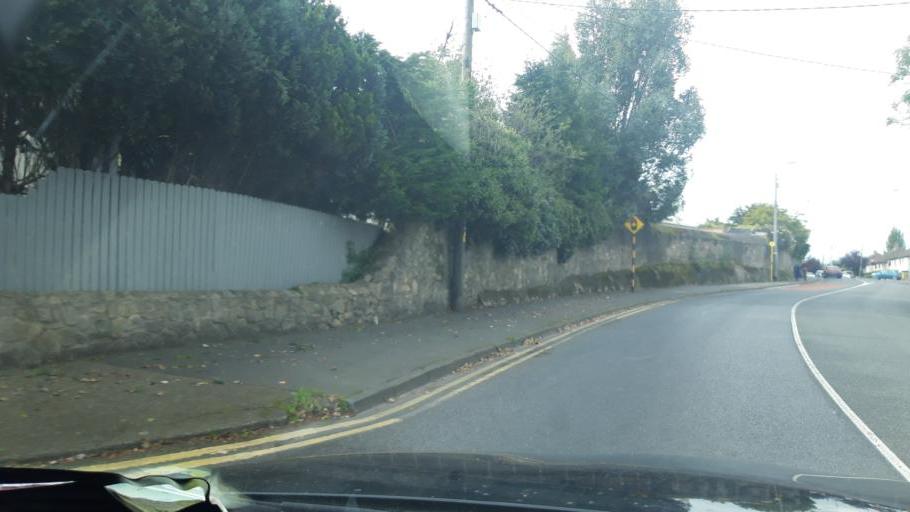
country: IE
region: Leinster
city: Cabinteely
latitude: 53.2643
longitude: -6.1584
